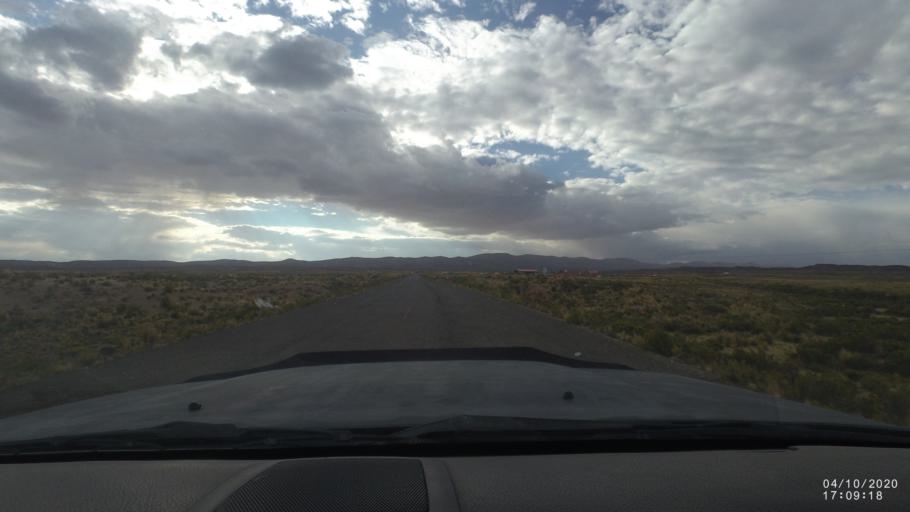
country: BO
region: Oruro
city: Oruro
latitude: -18.3399
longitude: -67.5815
